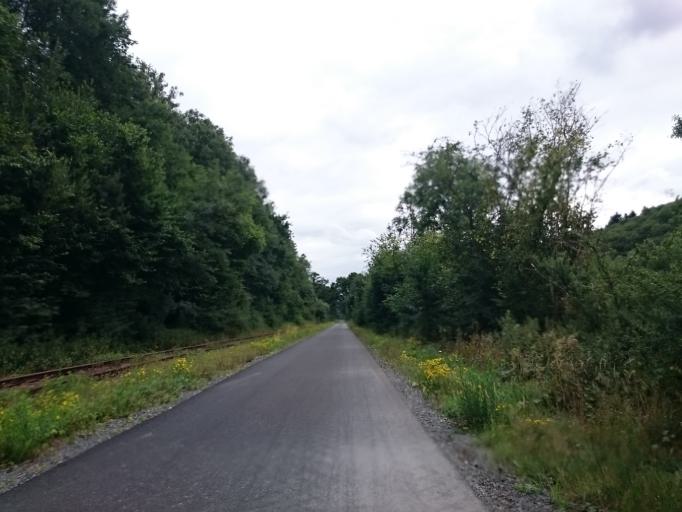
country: FR
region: Lower Normandy
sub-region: Departement du Calvados
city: Sainte-Honorine-du-Fay
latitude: 49.0417
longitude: -0.4631
